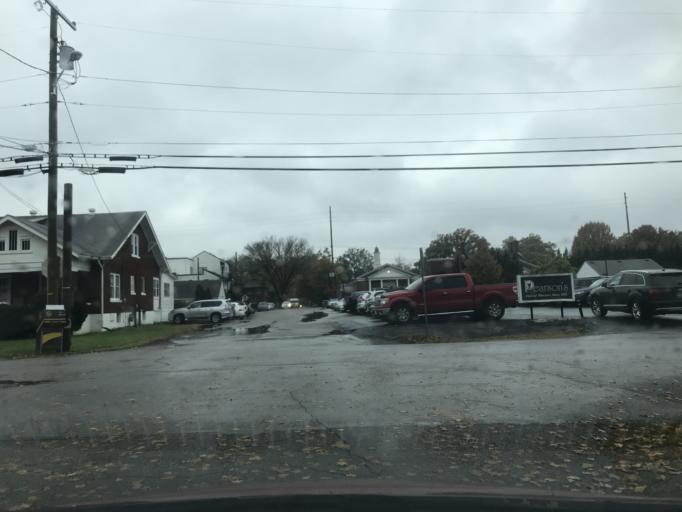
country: US
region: Kentucky
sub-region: Jefferson County
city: Saint Matthews
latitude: 38.2513
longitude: -85.6521
